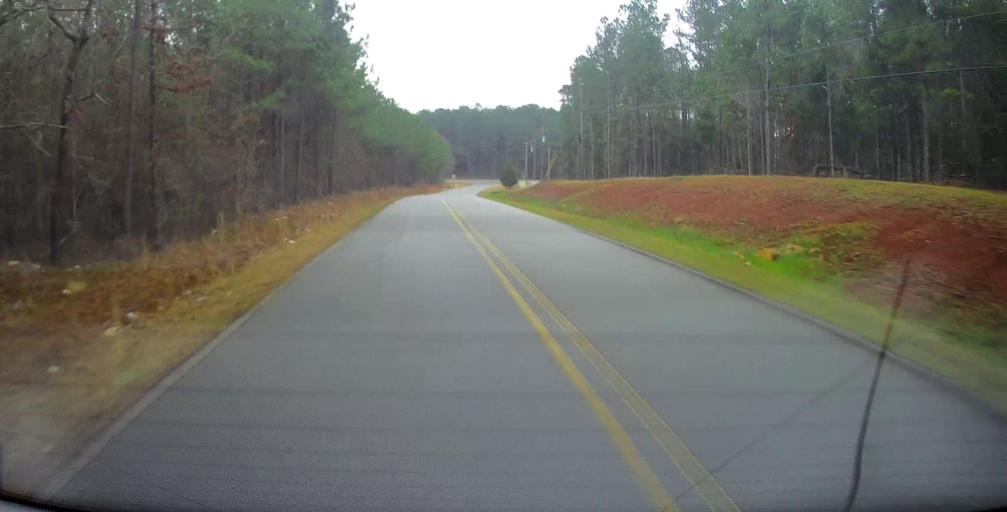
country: US
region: Georgia
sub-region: Monroe County
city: Forsyth
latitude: 33.0816
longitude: -83.9120
